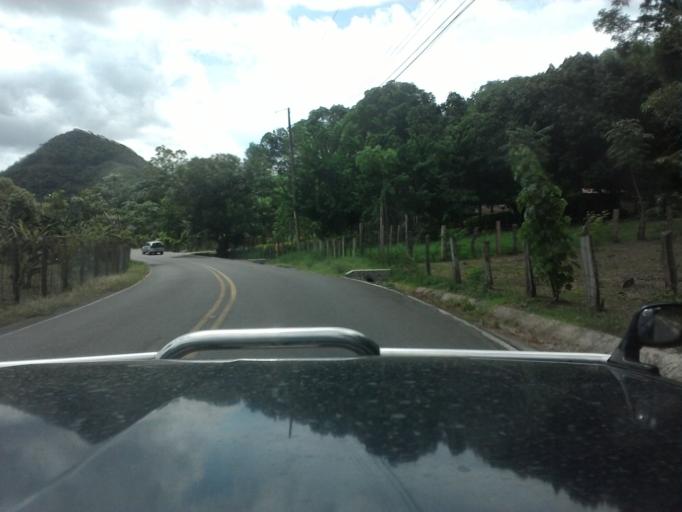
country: CR
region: Puntarenas
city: Miramar
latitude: 10.1762
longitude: -84.8464
